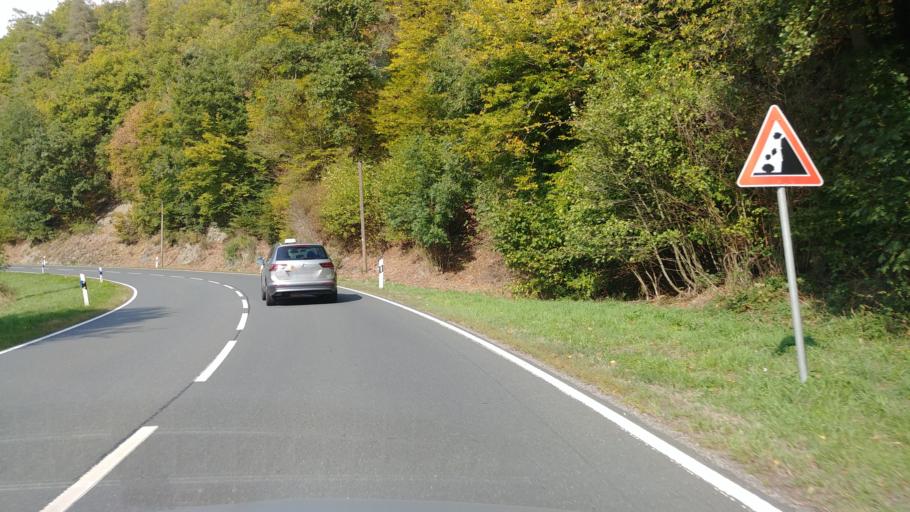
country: DE
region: Hesse
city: Burg Hohenstein
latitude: 50.1735
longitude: 8.0743
